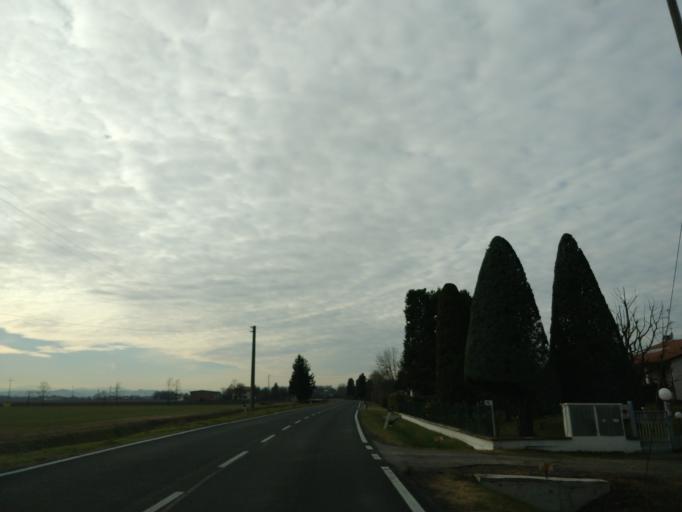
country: IT
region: Emilia-Romagna
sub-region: Provincia di Bologna
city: Argelato
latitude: 44.6291
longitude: 11.3409
